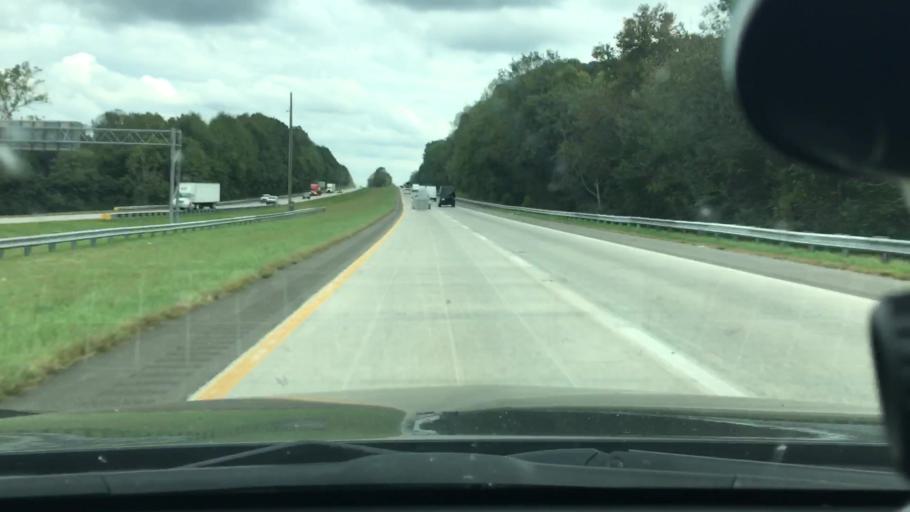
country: US
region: North Carolina
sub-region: Iredell County
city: Statesville
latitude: 35.8209
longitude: -80.8120
